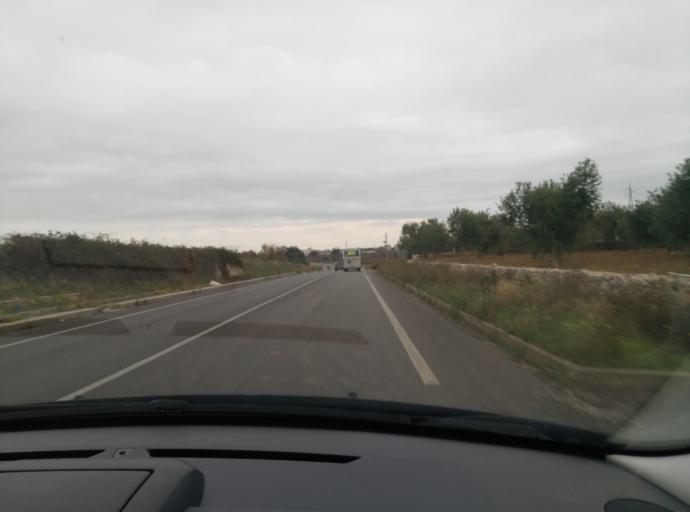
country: IT
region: Apulia
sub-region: Provincia di Bari
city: Acquaviva delle Fonti
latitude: 40.8893
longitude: 16.8266
